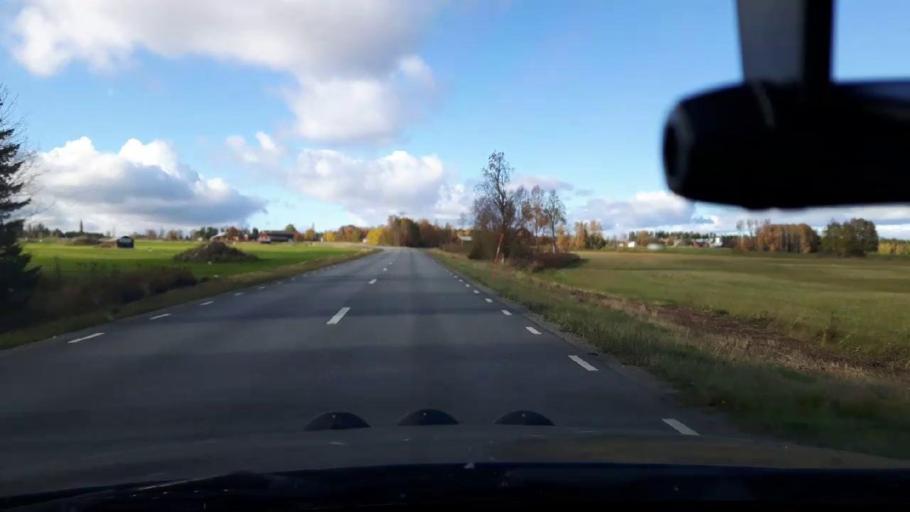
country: SE
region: Jaemtland
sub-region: Bergs Kommun
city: Hoverberg
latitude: 62.9885
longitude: 14.4329
